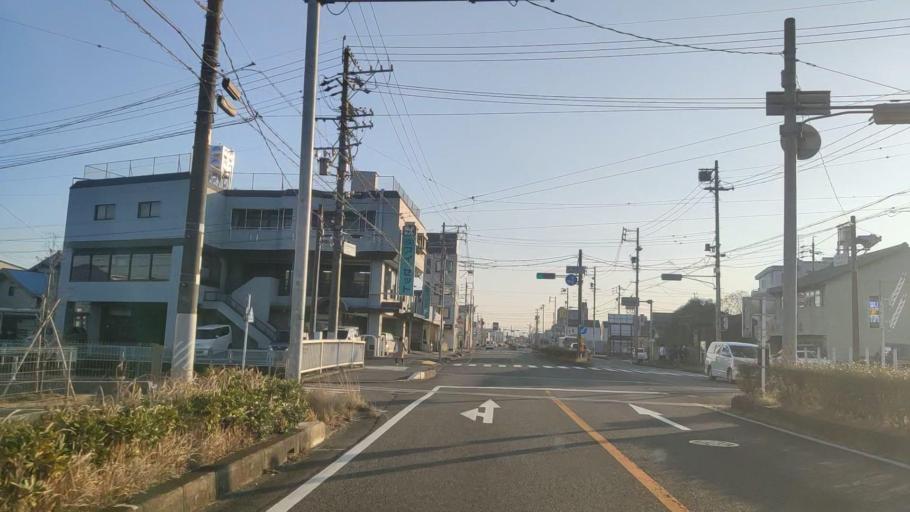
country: JP
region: Gifu
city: Gifu-shi
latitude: 35.4357
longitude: 136.7369
